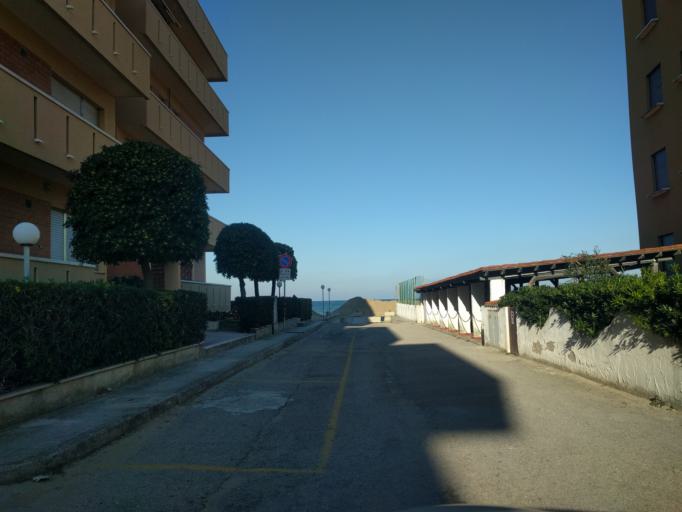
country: IT
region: The Marches
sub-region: Provincia di Pesaro e Urbino
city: Marotta
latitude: 43.7942
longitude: 13.1022
